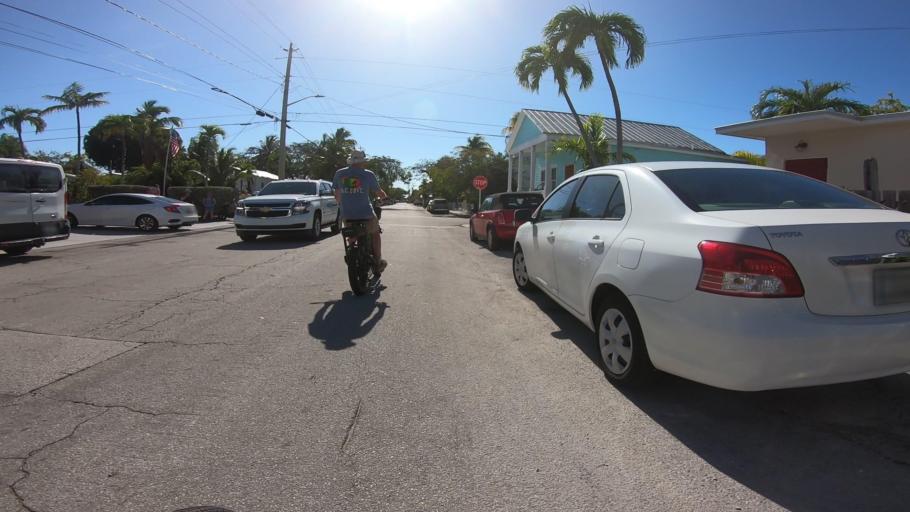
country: US
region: Florida
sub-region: Monroe County
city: Key West
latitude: 24.5523
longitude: -81.7930
